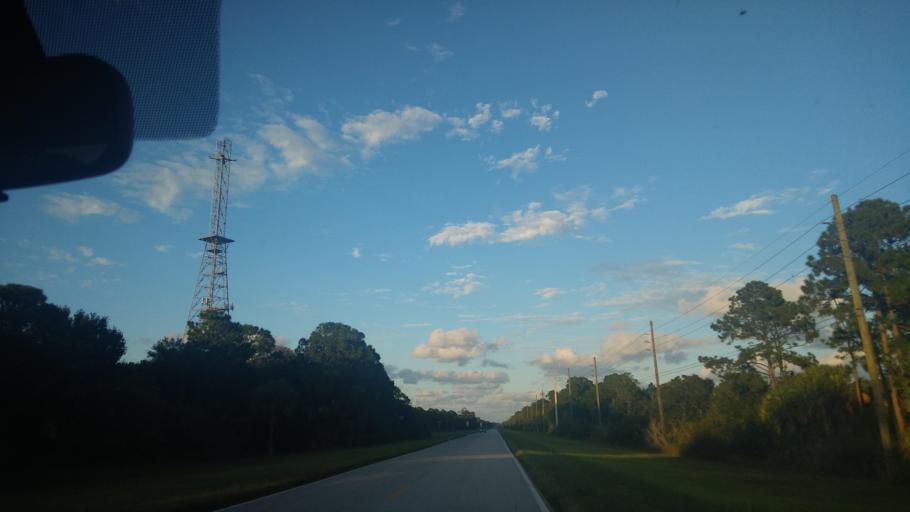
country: US
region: Florida
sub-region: Indian River County
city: Fellsmere
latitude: 27.7493
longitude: -80.6286
